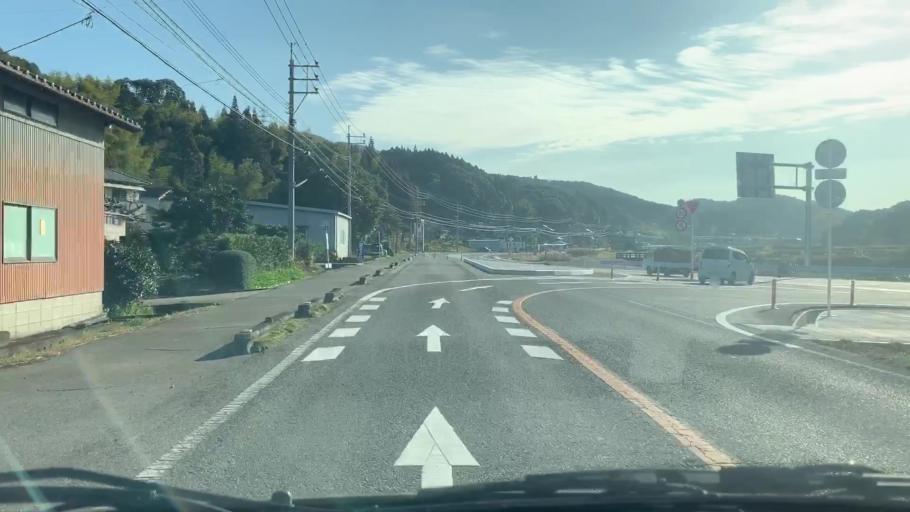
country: JP
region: Saga Prefecture
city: Takeocho-takeo
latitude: 33.2502
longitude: 129.9989
